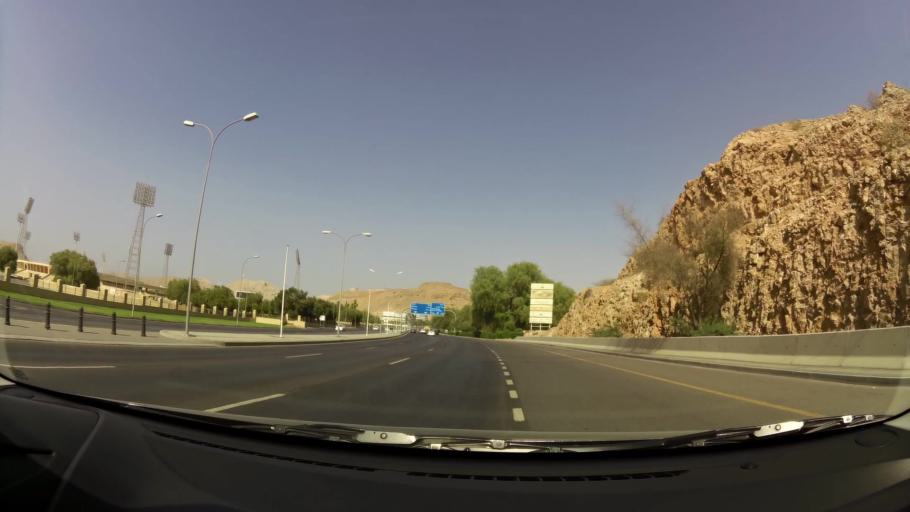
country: OM
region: Muhafazat Masqat
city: Muscat
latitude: 23.6068
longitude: 58.5043
